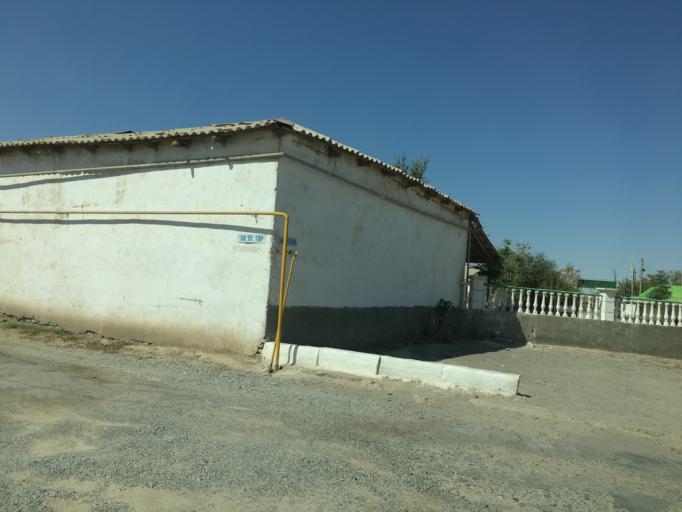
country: IR
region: Razavi Khorasan
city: Sarakhs
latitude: 36.5247
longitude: 61.2139
